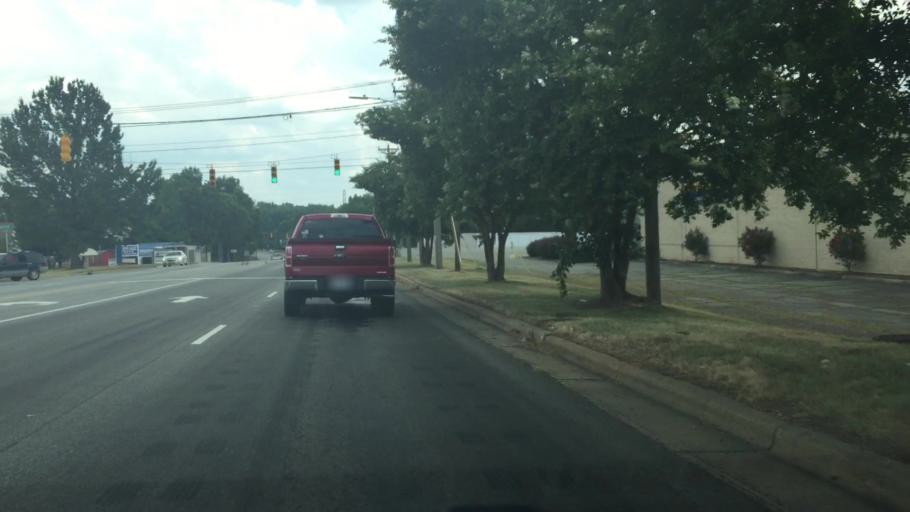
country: US
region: North Carolina
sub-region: Rowan County
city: Salisbury
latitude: 35.6785
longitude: -80.5052
